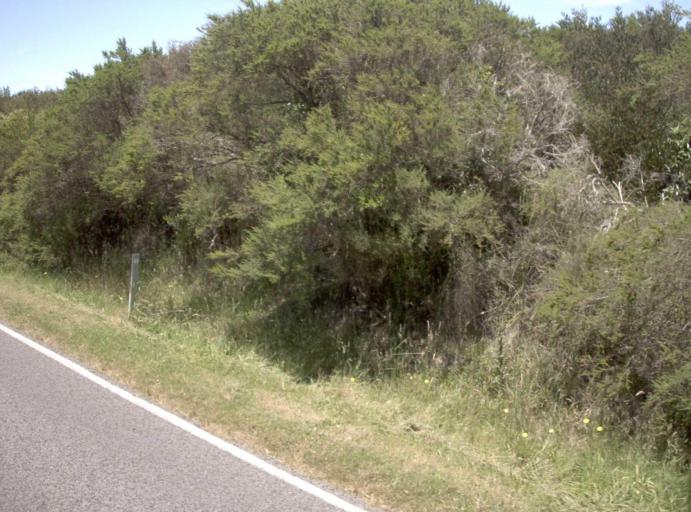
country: AU
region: Victoria
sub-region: Bass Coast
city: North Wonthaggi
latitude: -38.7690
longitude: 146.1575
